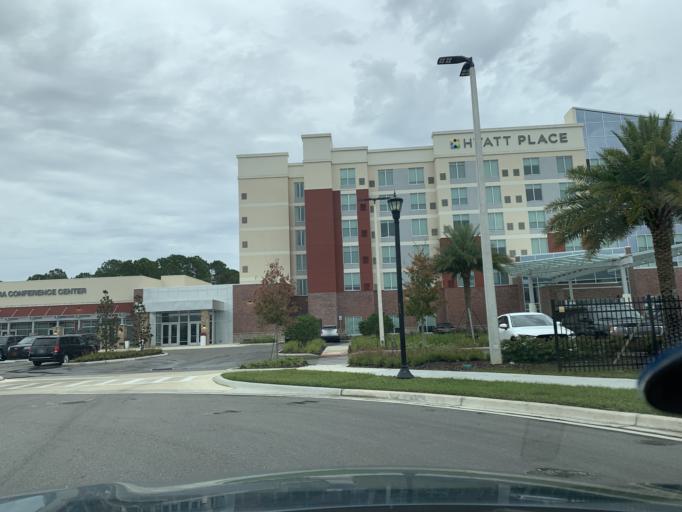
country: US
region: Florida
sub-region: Hillsborough County
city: Pebble Creek
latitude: 28.1961
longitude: -82.3877
